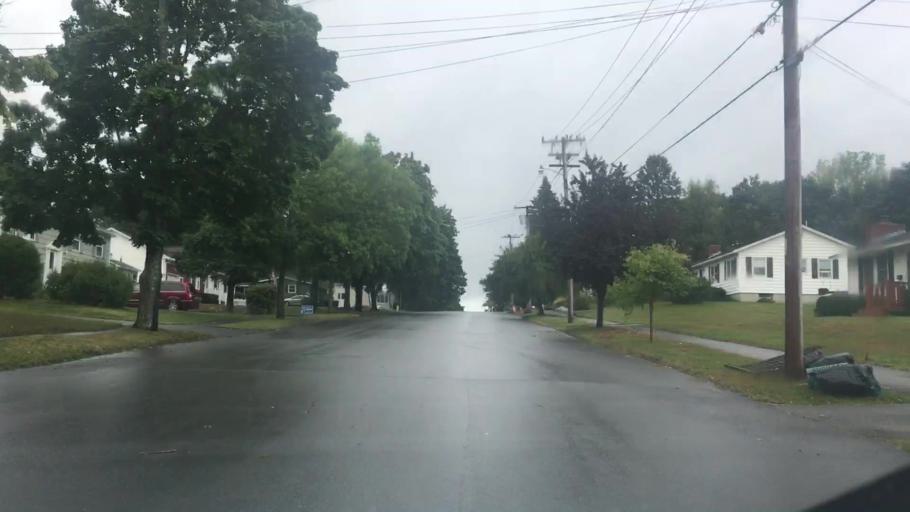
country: US
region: Maine
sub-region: Penobscot County
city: Brewer
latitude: 44.8187
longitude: -68.7608
